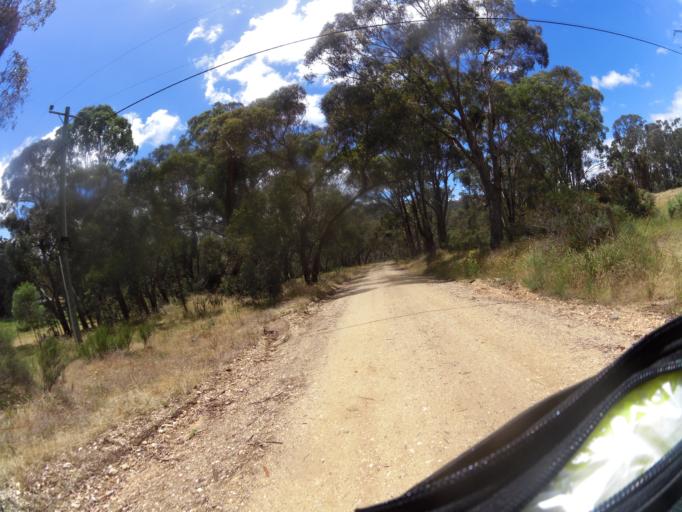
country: AU
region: Victoria
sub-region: Mount Alexander
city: Castlemaine
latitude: -37.0589
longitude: 144.2708
